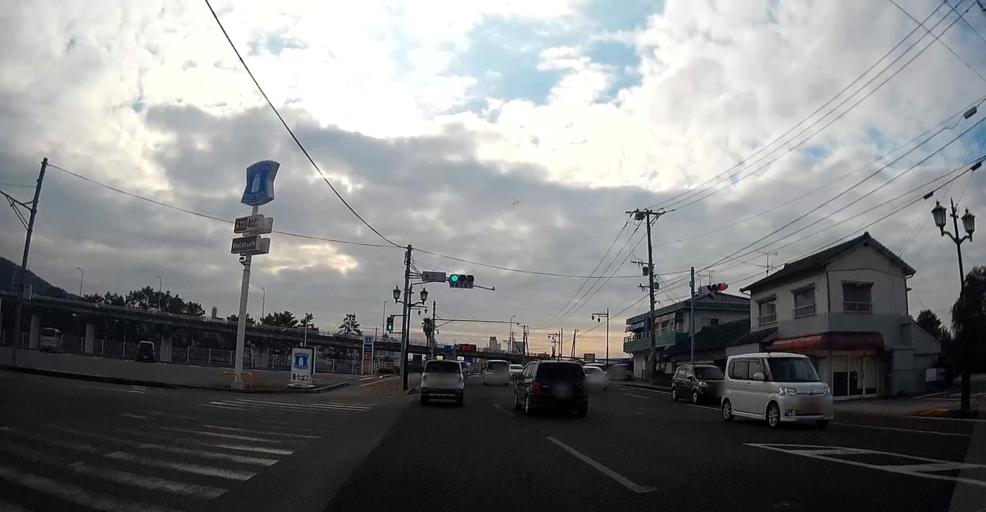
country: JP
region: Kumamoto
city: Hondo
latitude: 32.4481
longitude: 130.2002
